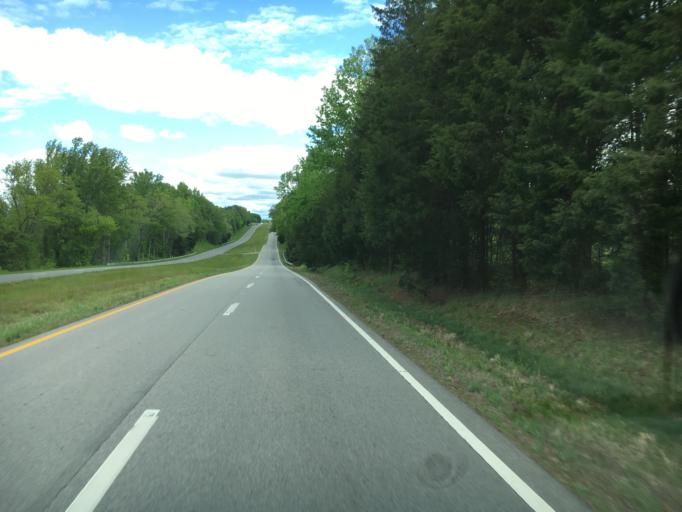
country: US
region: Virginia
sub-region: Halifax County
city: Mountain Road
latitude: 36.6137
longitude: -79.0538
